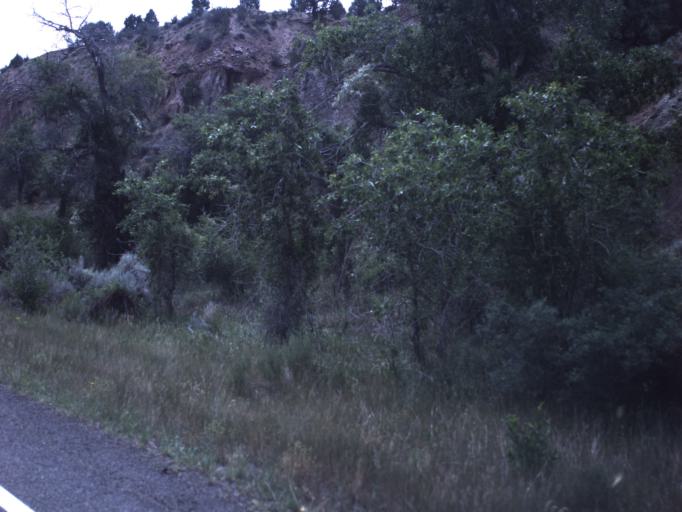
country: US
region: Utah
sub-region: Daggett County
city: Manila
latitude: 40.9267
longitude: -109.7187
